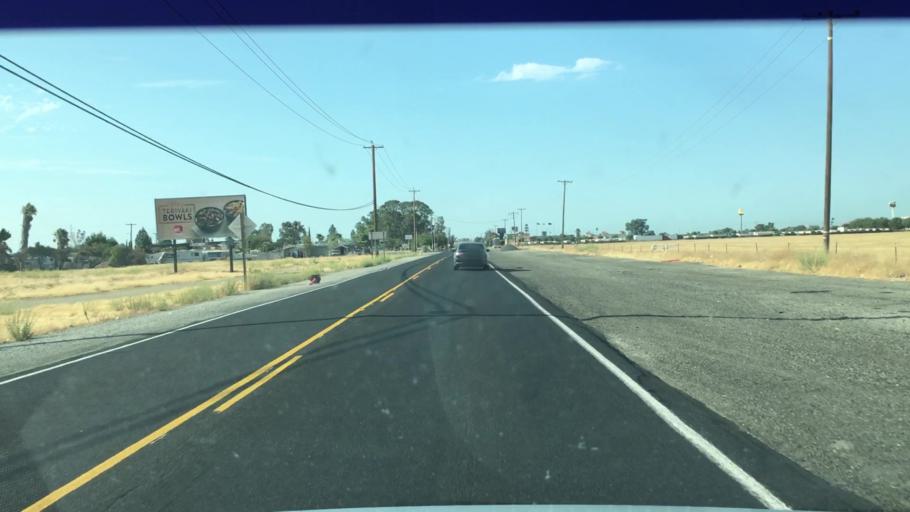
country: US
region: California
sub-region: Merced County
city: Gustine
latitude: 37.0943
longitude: -121.0160
